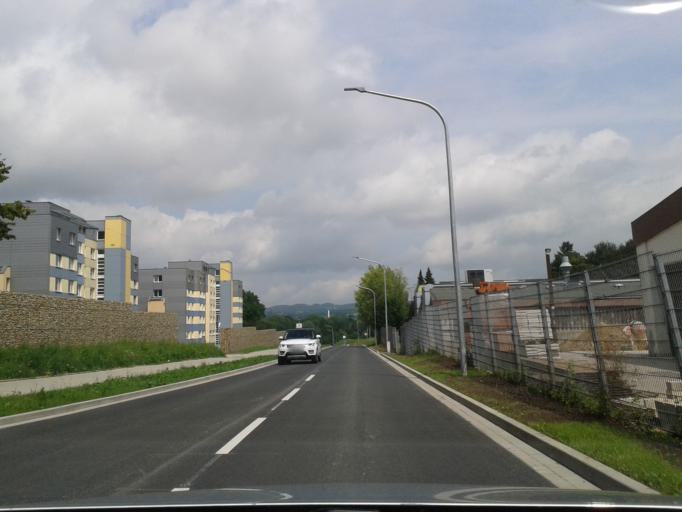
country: DE
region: North Rhine-Westphalia
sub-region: Regierungsbezirk Detmold
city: Lemgo
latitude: 52.0185
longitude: 8.9074
